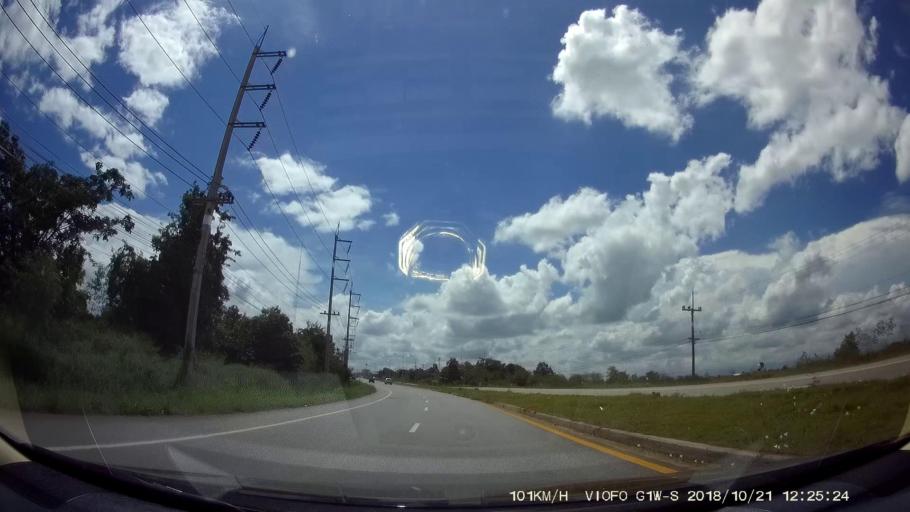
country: TH
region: Nakhon Ratchasima
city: Dan Khun Thot
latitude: 15.2219
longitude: 101.7721
